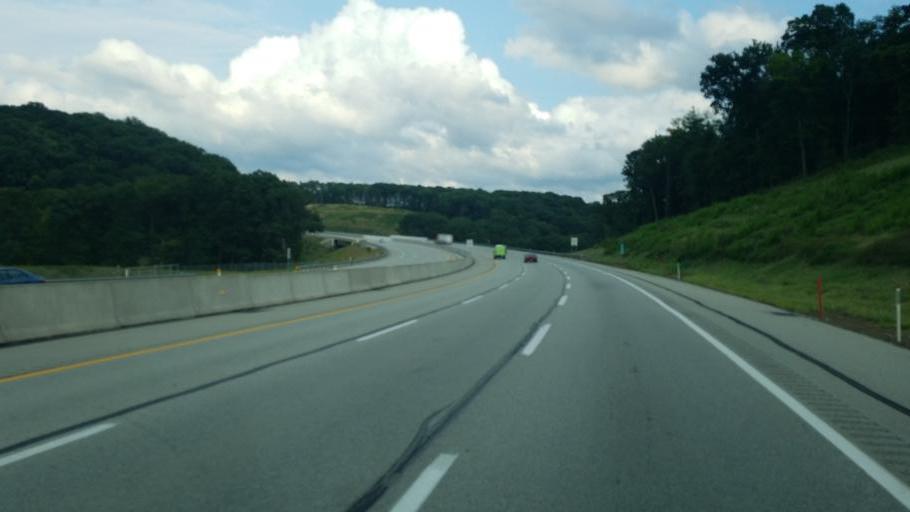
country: US
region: Pennsylvania
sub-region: Allegheny County
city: Bradford Woods
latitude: 40.6445
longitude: -80.0322
